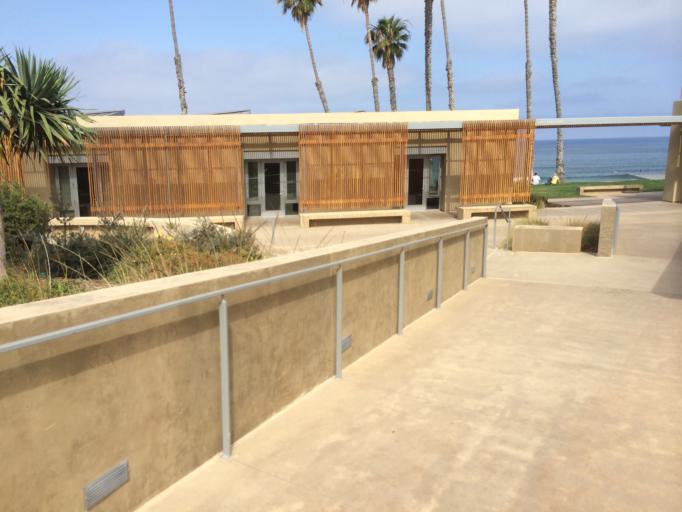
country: US
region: California
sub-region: San Diego County
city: La Jolla
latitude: 32.8642
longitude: -117.2540
